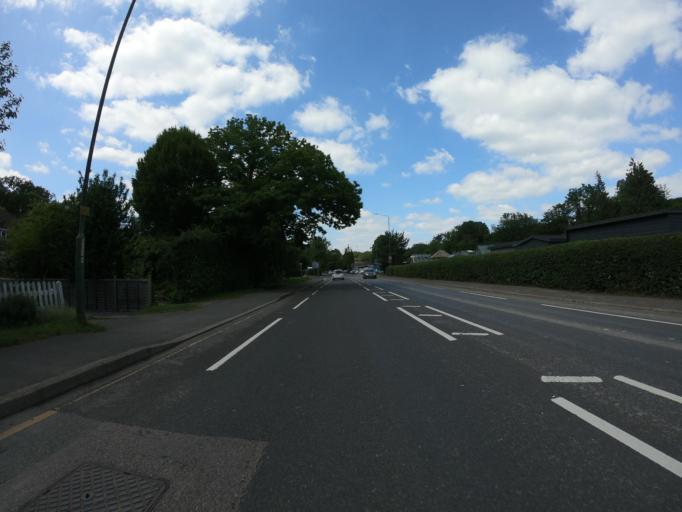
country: GB
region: England
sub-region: Kent
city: Halstead
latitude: 51.3435
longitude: 0.1376
